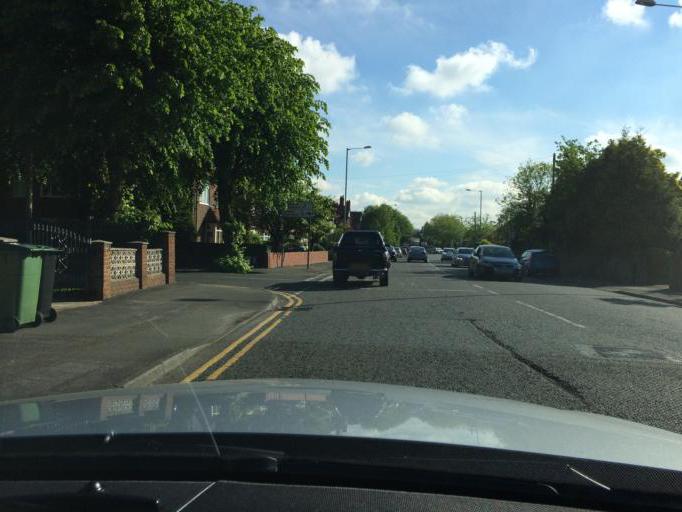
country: GB
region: England
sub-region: Borough of Stockport
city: Cheadle Hulme
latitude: 53.3774
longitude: -2.1924
